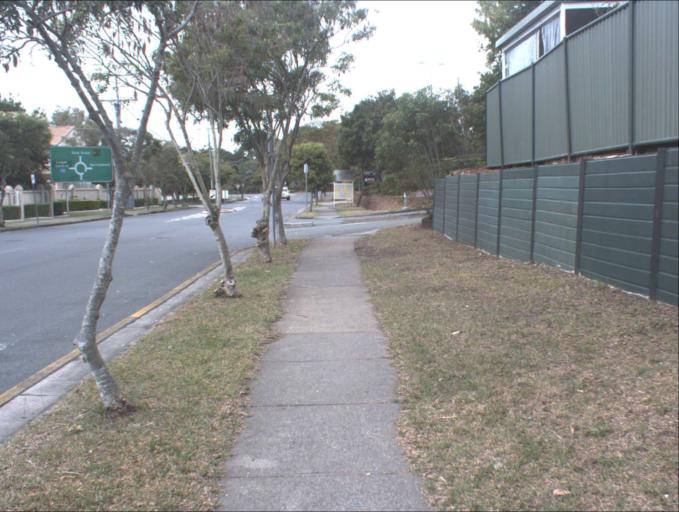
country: AU
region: Queensland
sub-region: Logan
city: Slacks Creek
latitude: -27.6323
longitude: 153.1389
